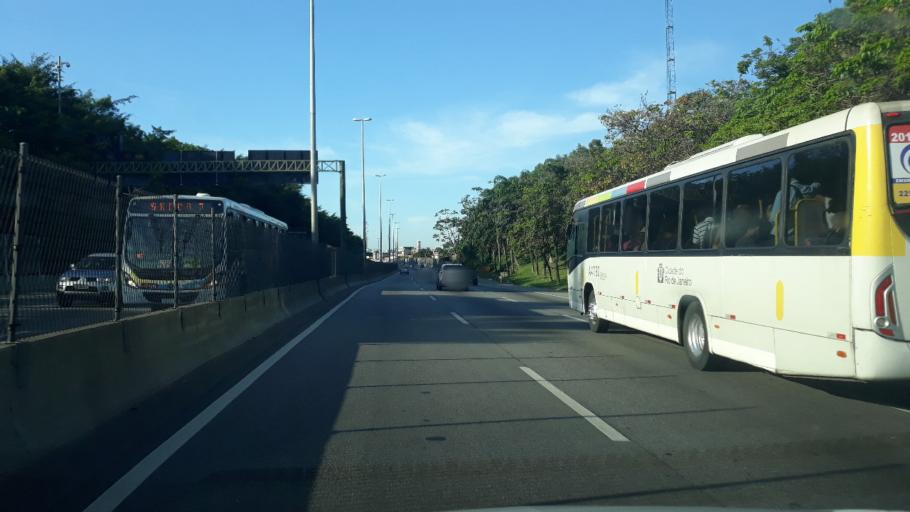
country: BR
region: Rio de Janeiro
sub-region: Sao Joao De Meriti
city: Sao Joao de Meriti
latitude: -22.9467
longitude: -43.3548
